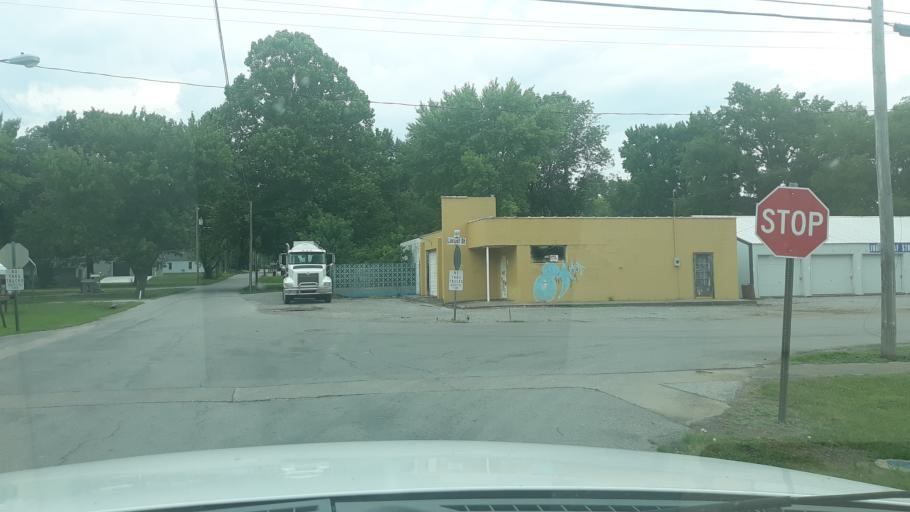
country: US
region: Illinois
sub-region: Saline County
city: Eldorado
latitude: 37.8072
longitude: -88.4566
